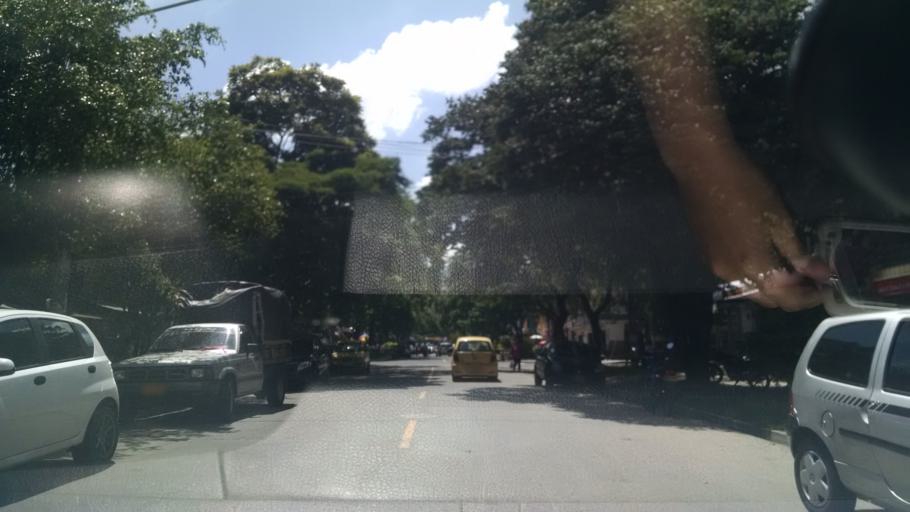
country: CO
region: Antioquia
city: Medellin
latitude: 6.2588
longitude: -75.6137
